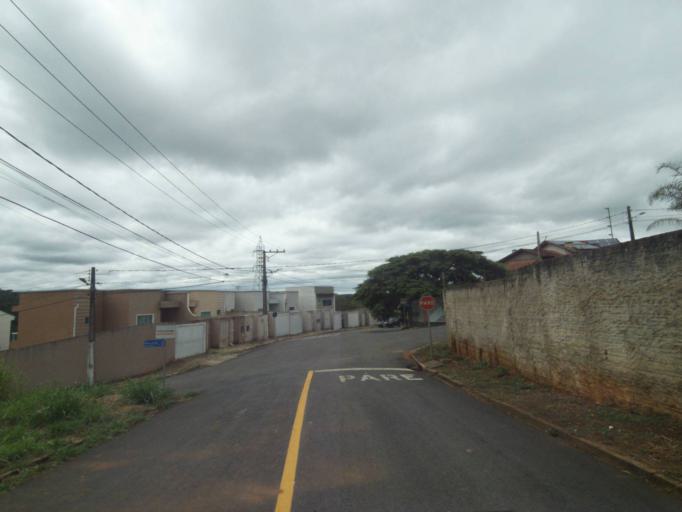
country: BR
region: Parana
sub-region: Telemaco Borba
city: Telemaco Borba
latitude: -24.3320
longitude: -50.6075
